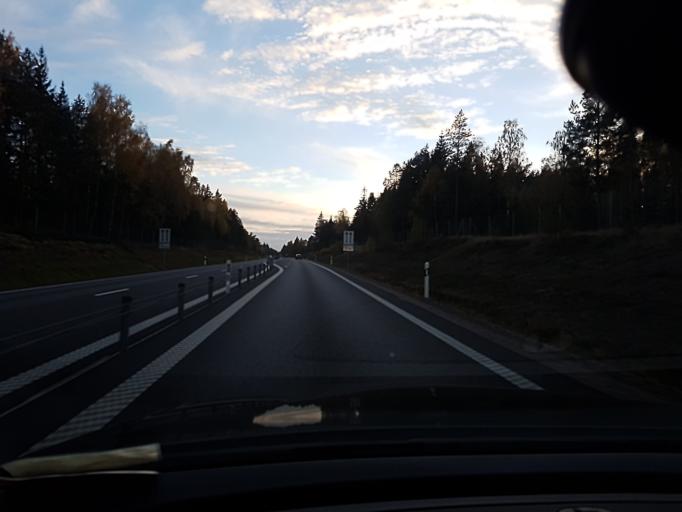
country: SE
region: Kronoberg
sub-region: Ljungby Kommun
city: Ljungby
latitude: 56.7828
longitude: 13.8223
